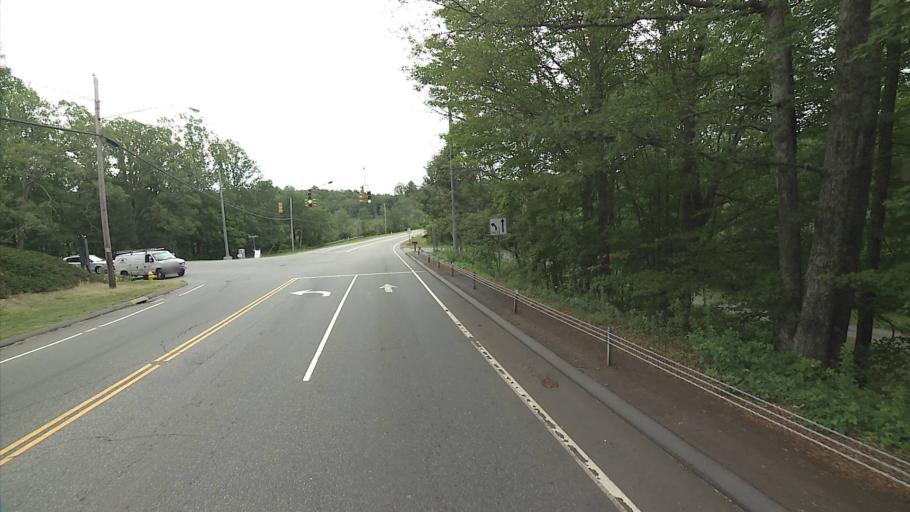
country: US
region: Connecticut
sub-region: New London County
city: Ledyard Center
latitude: 41.4395
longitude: -72.0154
